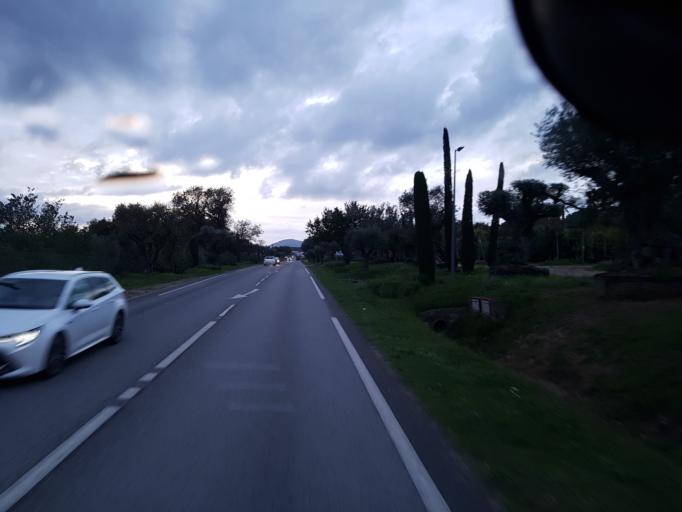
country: FR
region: Provence-Alpes-Cote d'Azur
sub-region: Departement du Var
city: Grimaud
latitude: 43.2700
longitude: 6.5394
